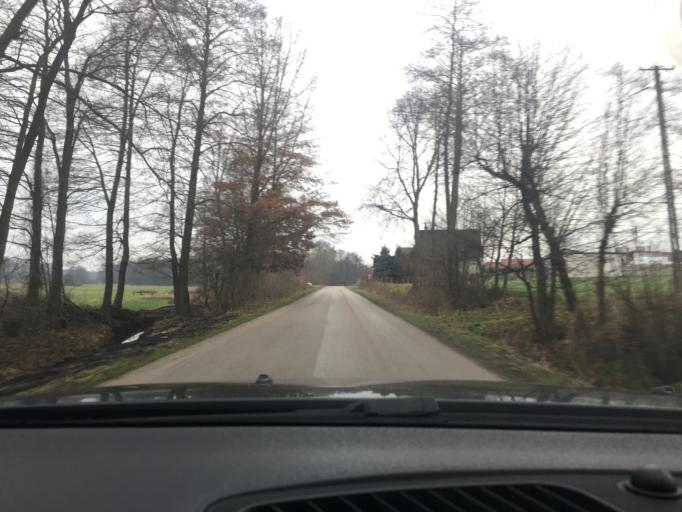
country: PL
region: Swietokrzyskie
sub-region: Powiat jedrzejowski
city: Imielno
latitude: 50.6421
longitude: 20.4034
